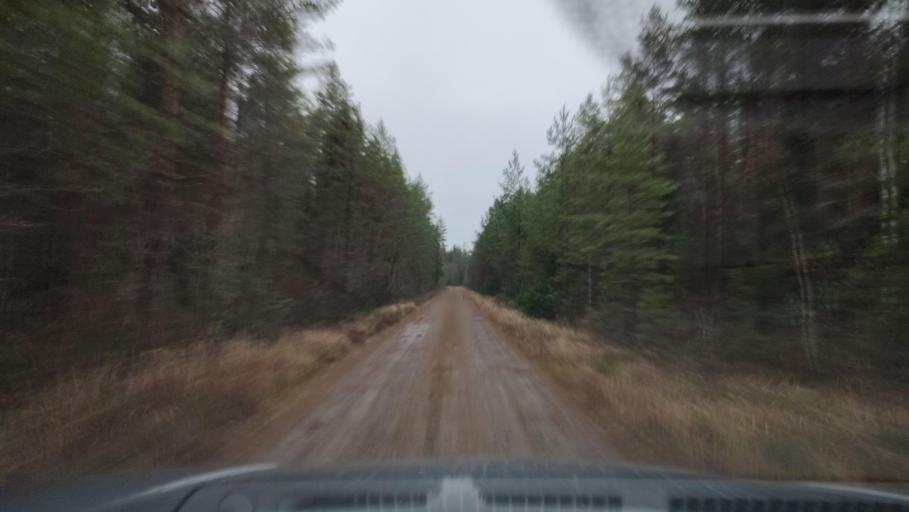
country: FI
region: Southern Ostrobothnia
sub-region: Suupohja
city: Karijoki
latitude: 62.1551
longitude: 21.5901
